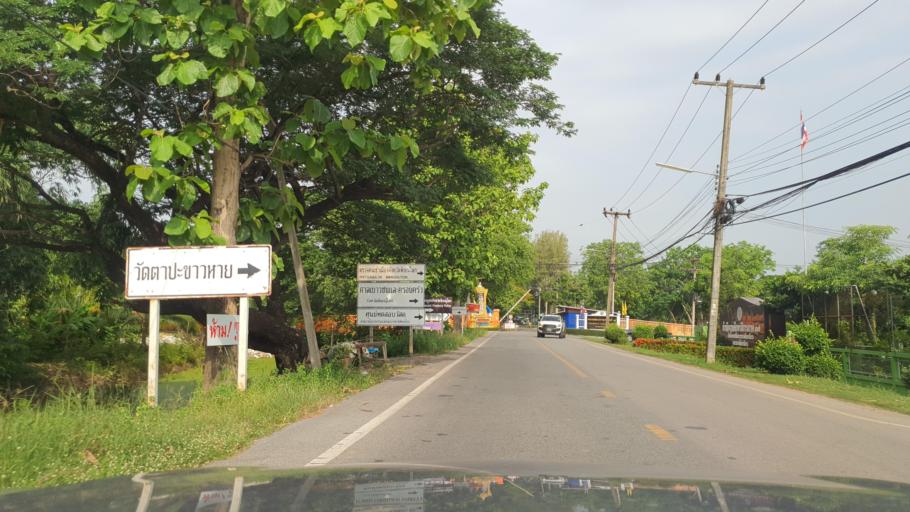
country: TH
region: Phitsanulok
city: Phitsanulok
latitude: 16.8425
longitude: 100.2612
